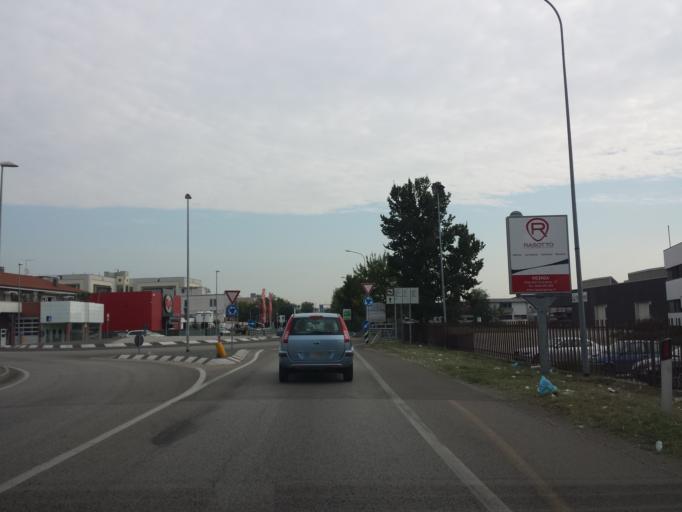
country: IT
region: Veneto
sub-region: Provincia di Vicenza
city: Creazzo
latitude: 45.5282
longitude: 11.4974
